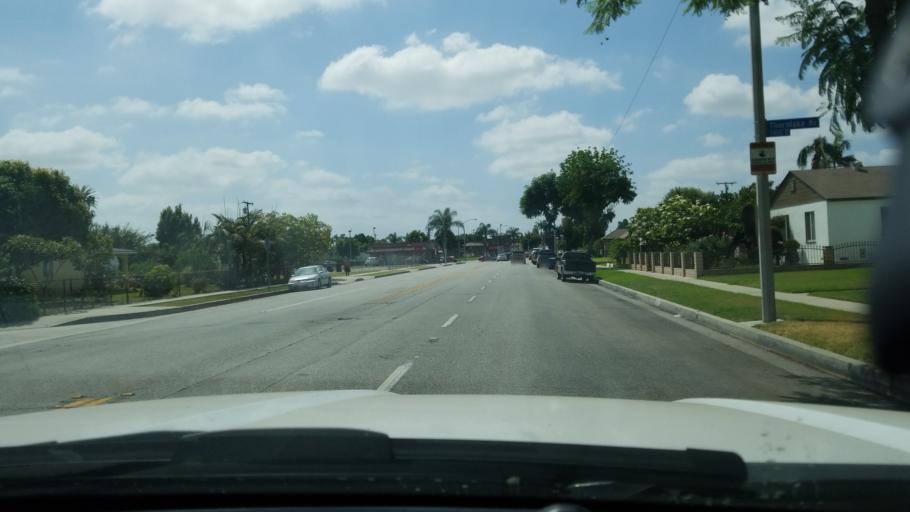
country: US
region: California
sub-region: Los Angeles County
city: West Whittier-Los Nietos
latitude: 33.9730
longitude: -118.0684
